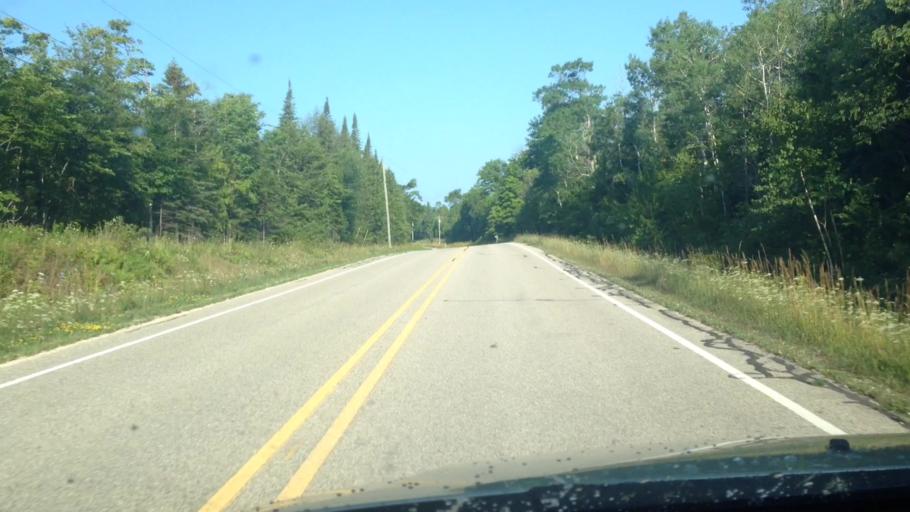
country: US
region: Michigan
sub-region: Mackinac County
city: Saint Ignace
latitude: 45.8936
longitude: -84.8088
